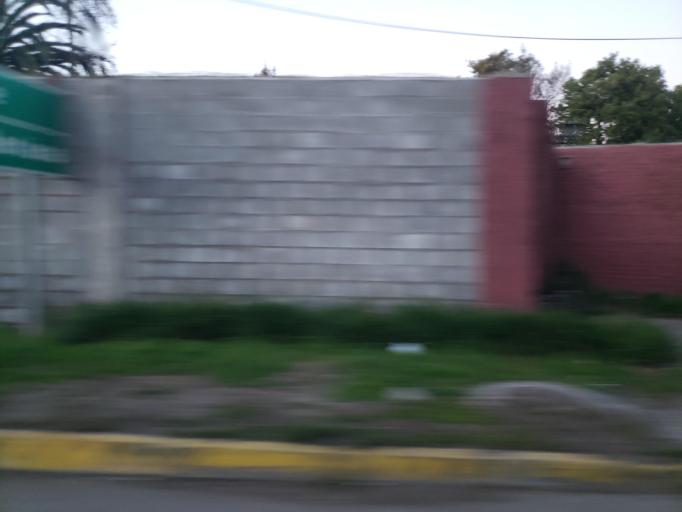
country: CL
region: Santiago Metropolitan
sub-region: Provincia de Talagante
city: El Monte
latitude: -33.6872
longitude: -70.9740
